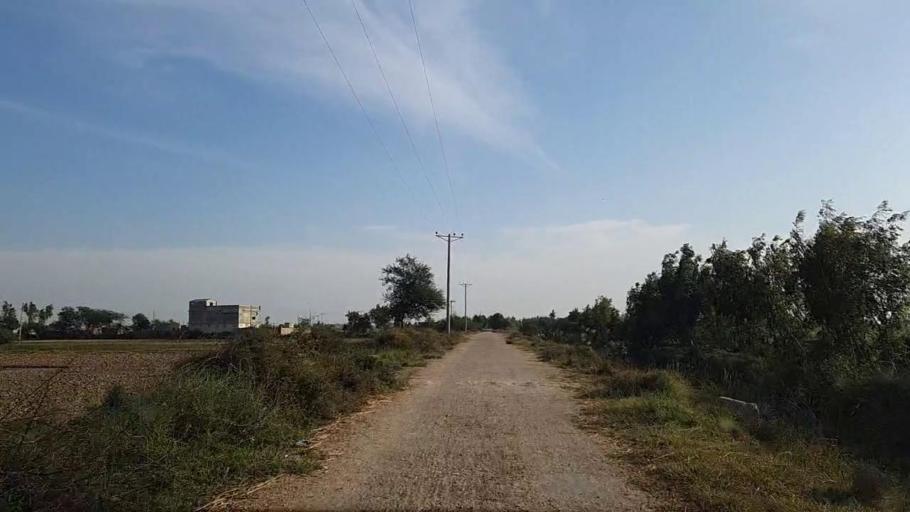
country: PK
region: Sindh
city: Daro Mehar
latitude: 24.6708
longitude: 68.1157
